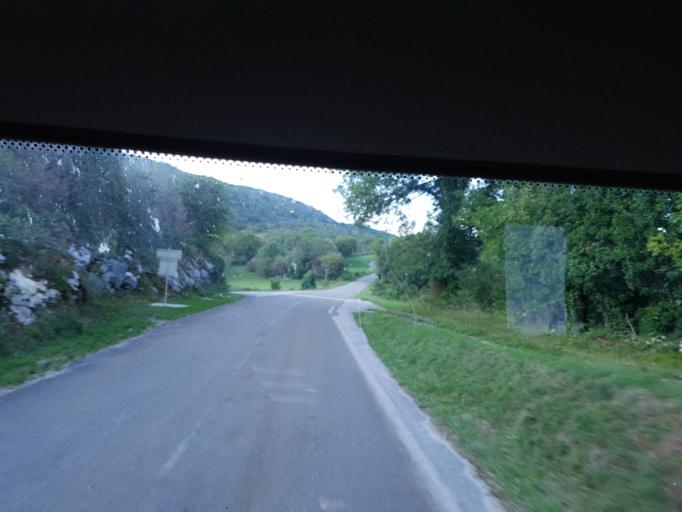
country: FR
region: Franche-Comte
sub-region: Departement du Jura
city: Moirans-en-Montagne
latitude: 46.4064
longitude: 5.6486
